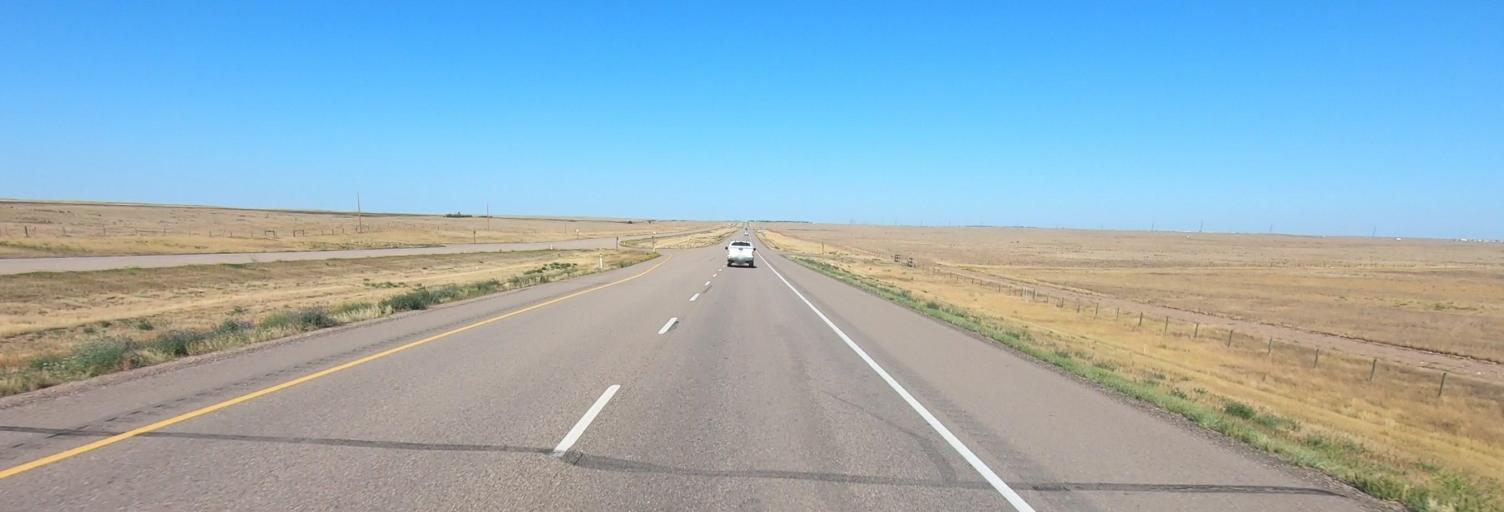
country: CA
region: Alberta
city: Medicine Hat
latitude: 50.1916
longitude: -111.0686
